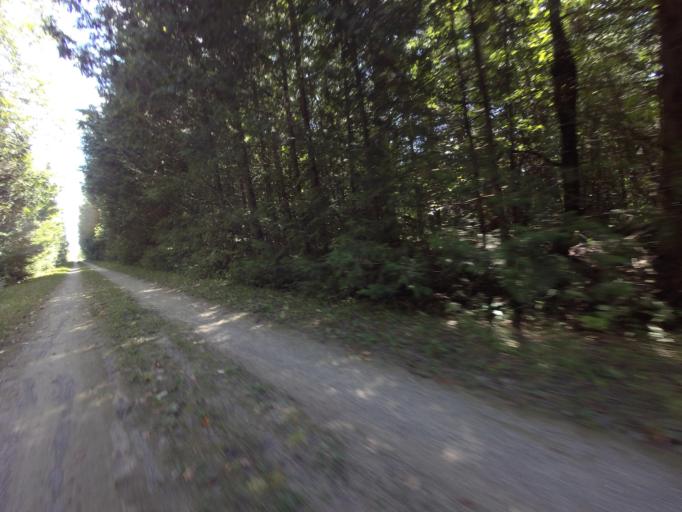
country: CA
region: Ontario
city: Orangeville
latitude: 43.7809
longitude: -80.2178
